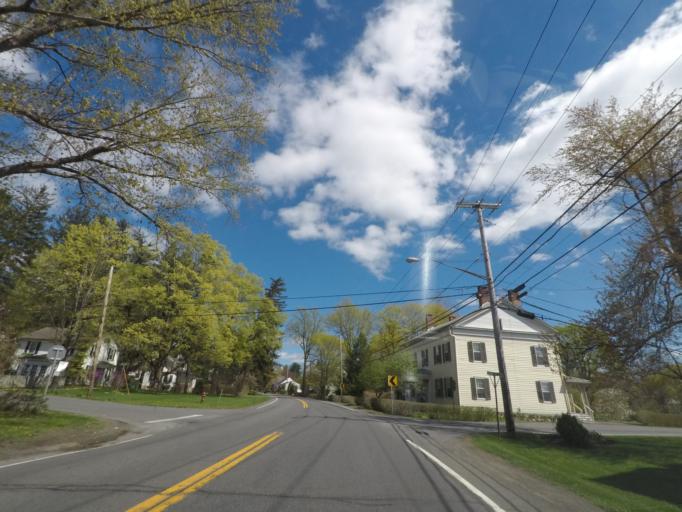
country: US
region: New York
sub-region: Columbia County
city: Oakdale
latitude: 42.2229
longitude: -73.7425
